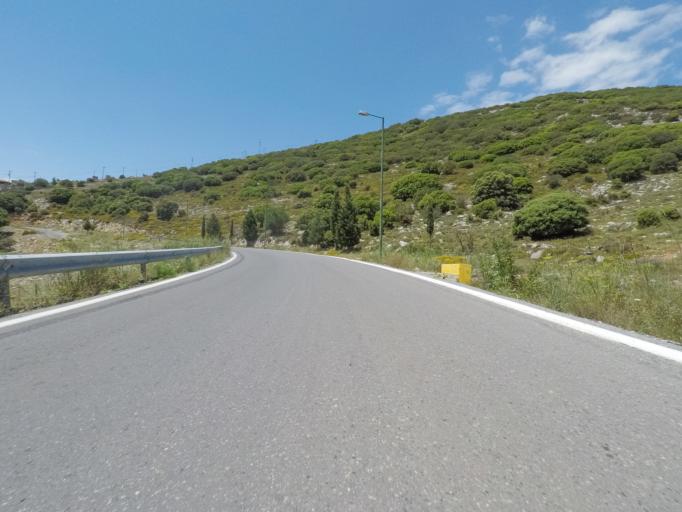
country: GR
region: Crete
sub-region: Nomos Irakleiou
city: Mokhos
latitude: 35.2028
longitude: 25.4585
